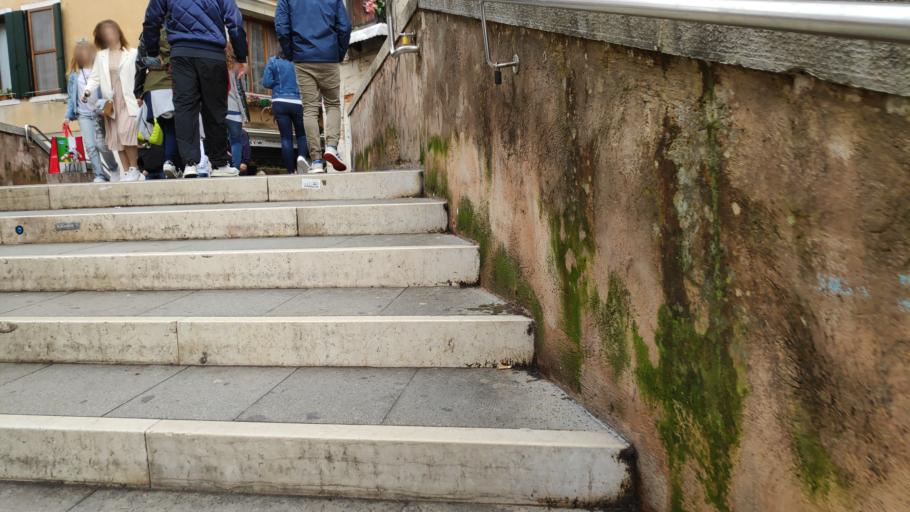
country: IT
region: Veneto
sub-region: Provincia di Venezia
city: Venice
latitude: 45.4433
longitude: 12.3315
